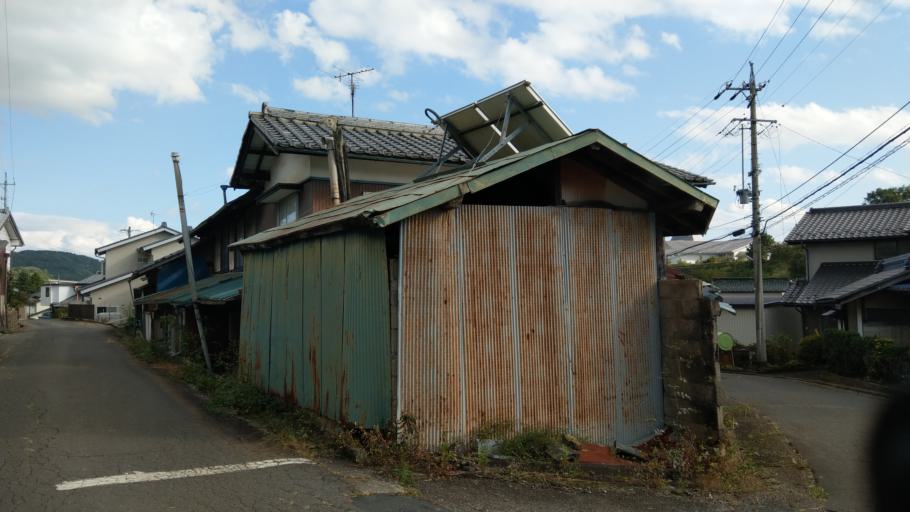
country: JP
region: Nagano
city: Komoro
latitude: 36.3466
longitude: 138.4191
